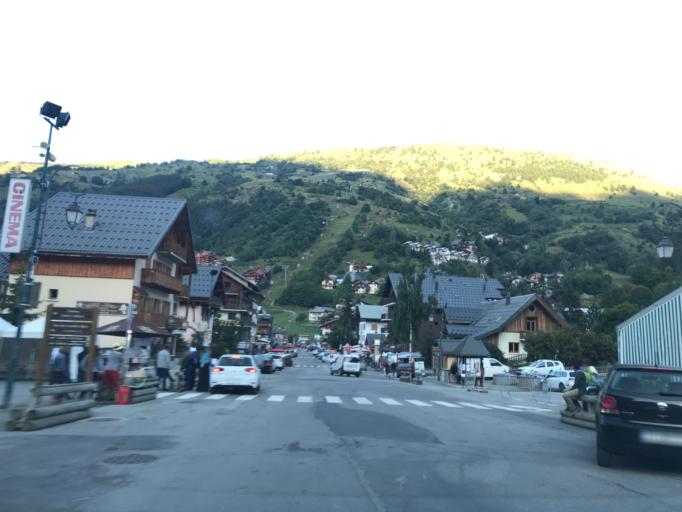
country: FR
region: Rhone-Alpes
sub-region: Departement de la Savoie
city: Valloire
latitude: 45.1641
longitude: 6.4269
